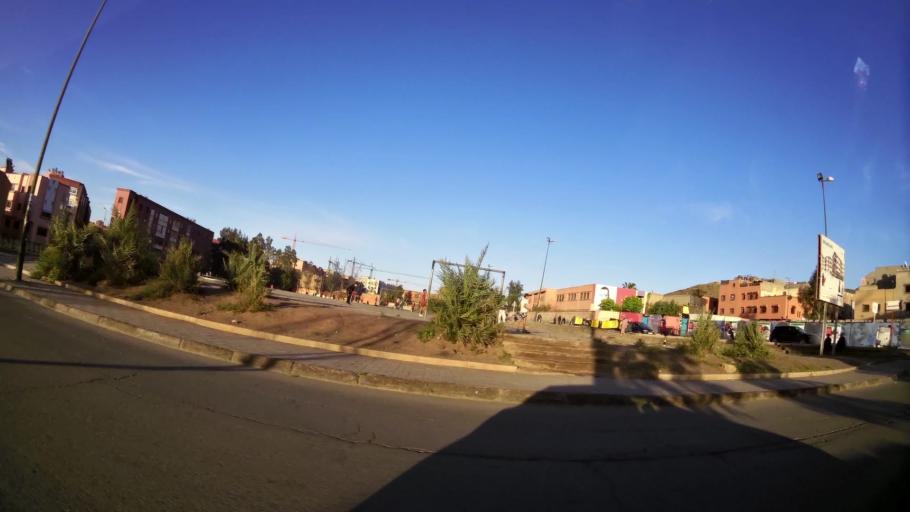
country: MA
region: Marrakech-Tensift-Al Haouz
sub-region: Marrakech
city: Marrakesh
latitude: 31.6530
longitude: -8.0319
